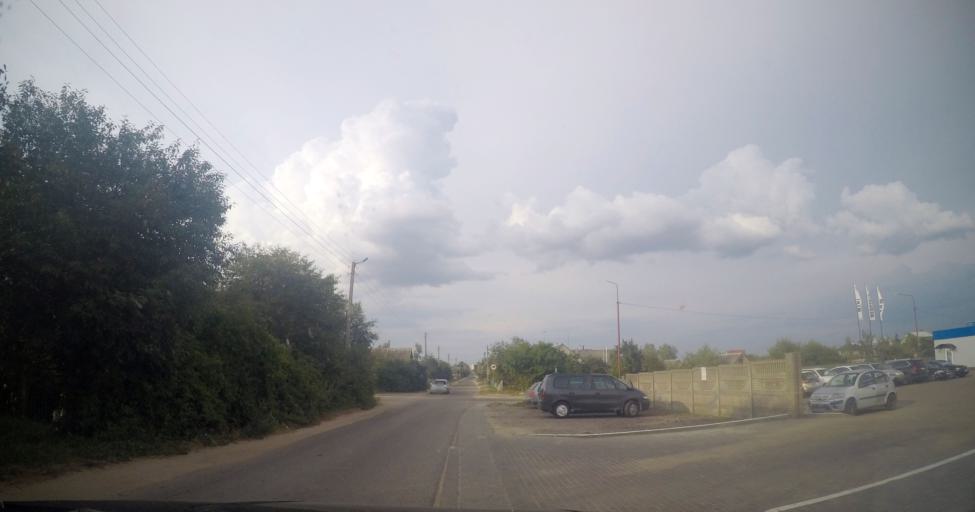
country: BY
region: Grodnenskaya
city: Hrodna
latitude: 53.6242
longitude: 23.8376
